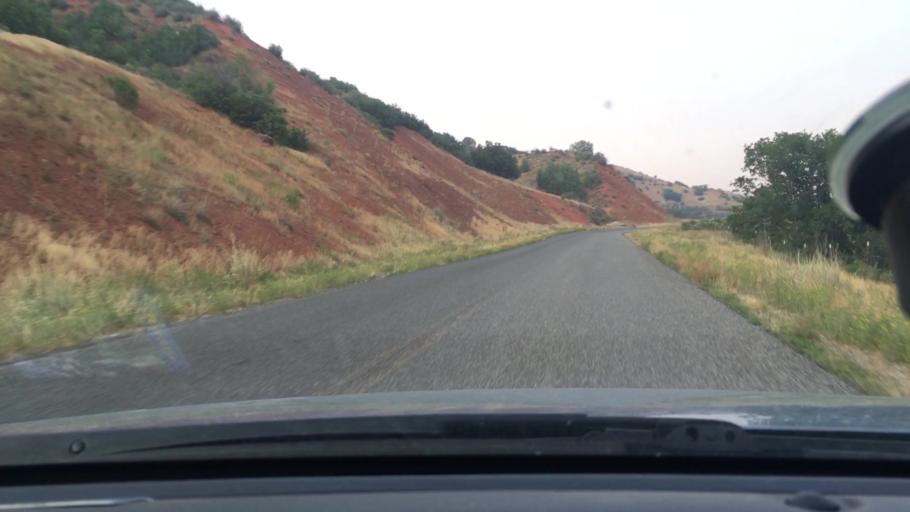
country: US
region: Utah
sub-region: Utah County
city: Mapleton
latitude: 40.0364
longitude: -111.4935
